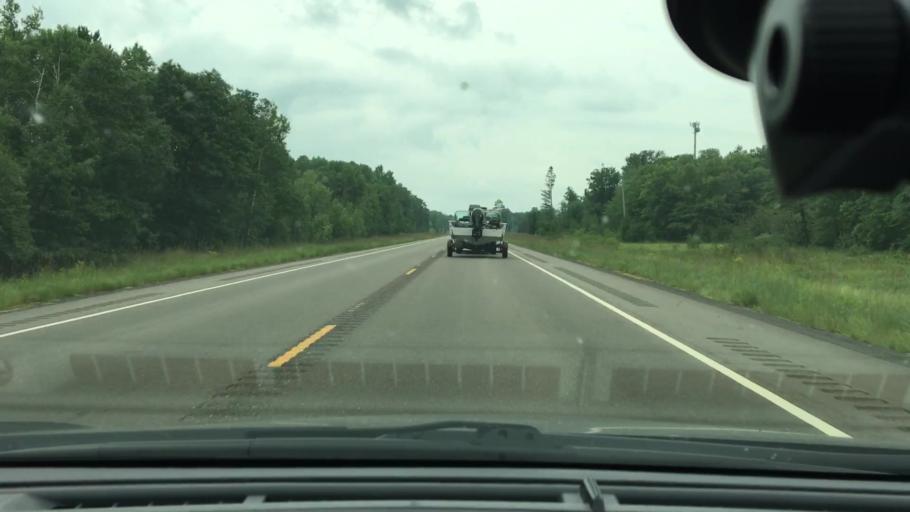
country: US
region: Minnesota
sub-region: Crow Wing County
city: Crosby
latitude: 46.5833
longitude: -93.9527
